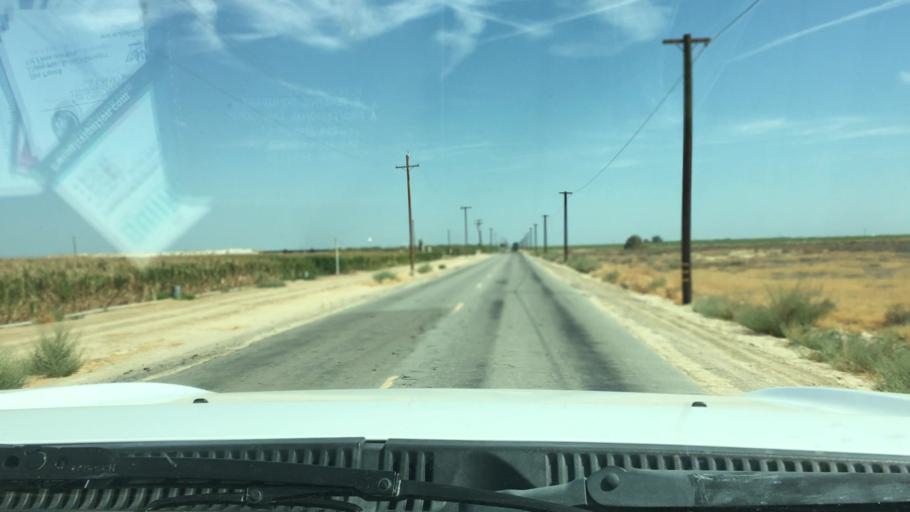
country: US
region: California
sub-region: Kern County
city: Shafter
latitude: 35.4468
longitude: -119.3681
